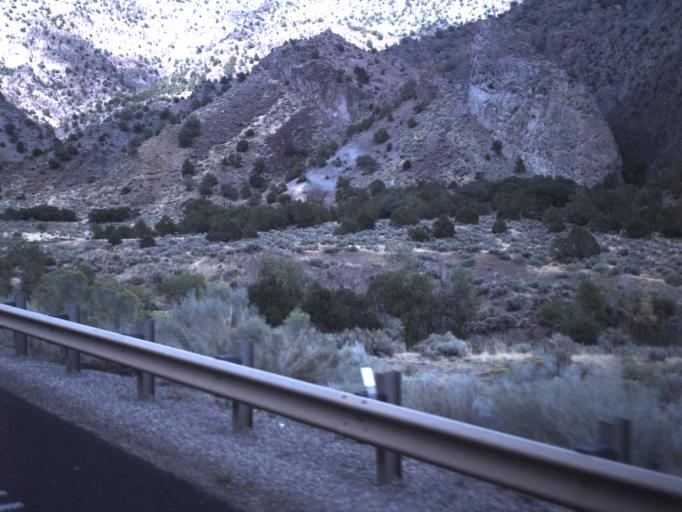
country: US
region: Utah
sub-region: Sevier County
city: Monroe
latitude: 38.5476
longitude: -112.2685
